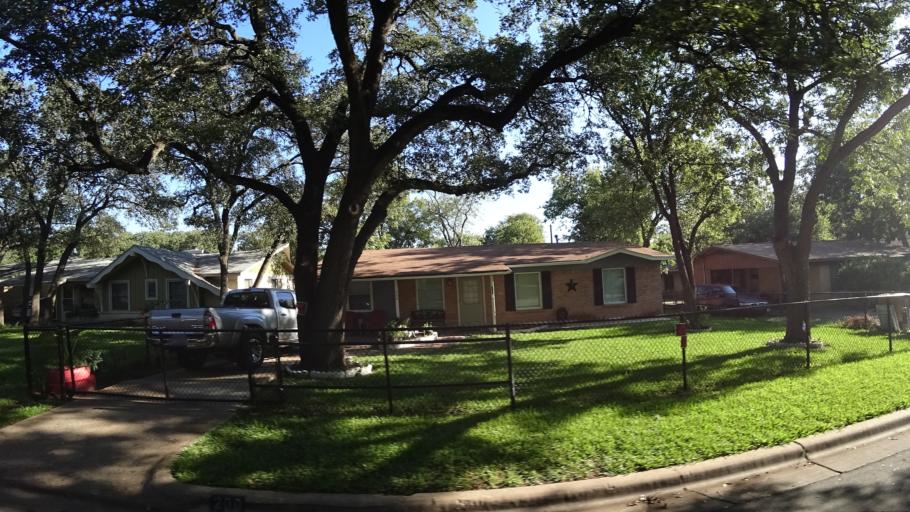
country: US
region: Texas
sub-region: Travis County
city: Austin
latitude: 30.3486
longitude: -97.7012
